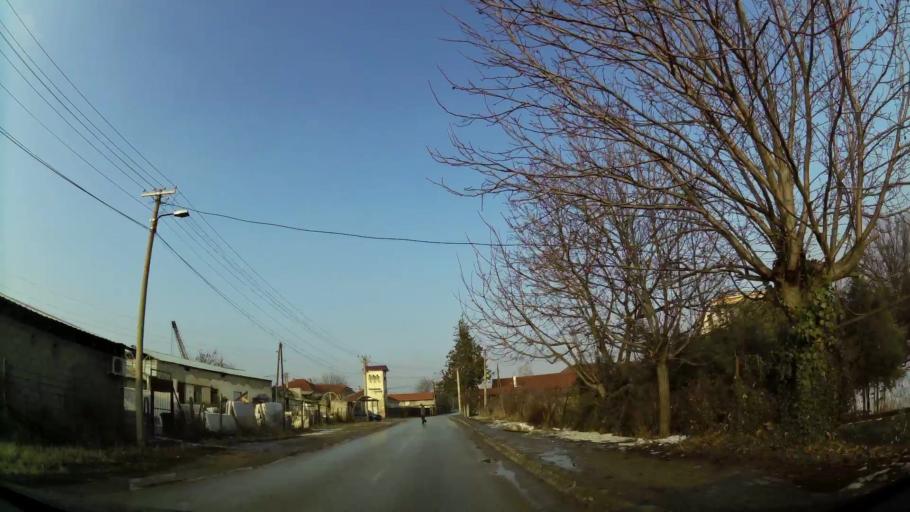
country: MK
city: Miladinovci
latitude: 41.9862
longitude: 21.6514
